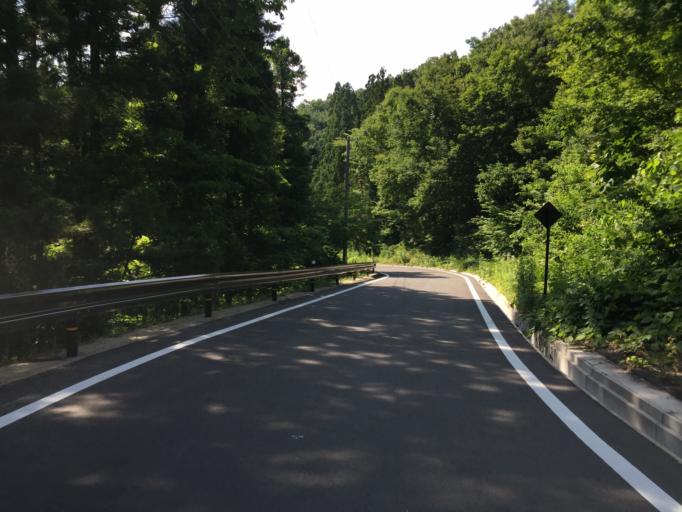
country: JP
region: Fukushima
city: Yanagawamachi-saiwaicho
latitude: 37.7853
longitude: 140.6601
